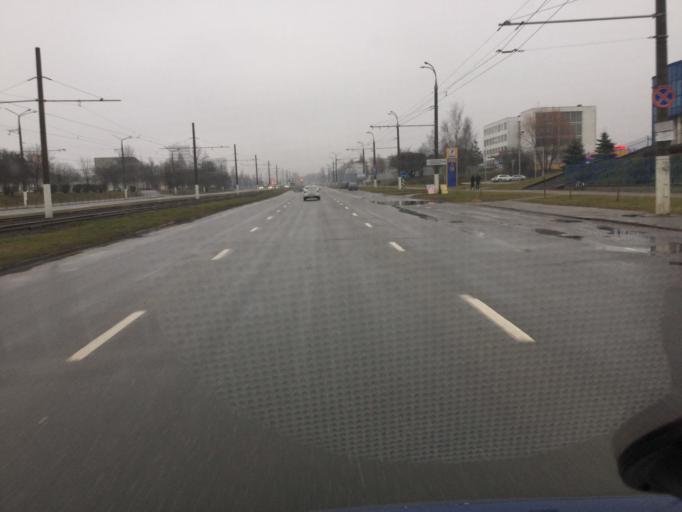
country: BY
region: Vitebsk
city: Vitebsk
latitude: 55.1603
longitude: 30.2361
